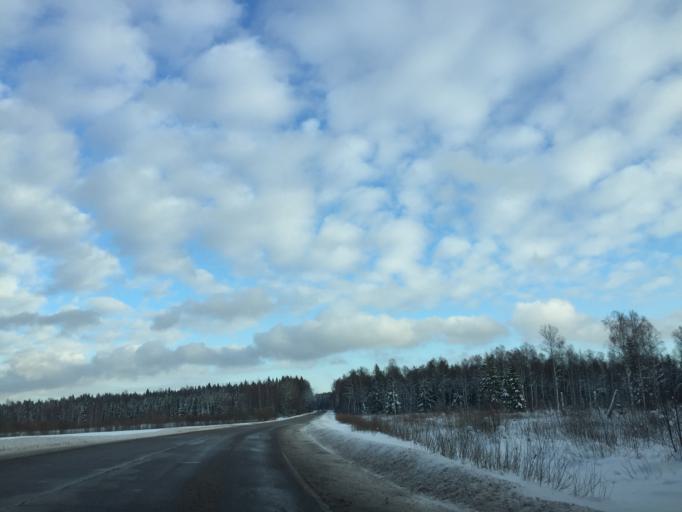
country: LV
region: Ropazu
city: Ropazi
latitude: 56.9980
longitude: 24.6502
